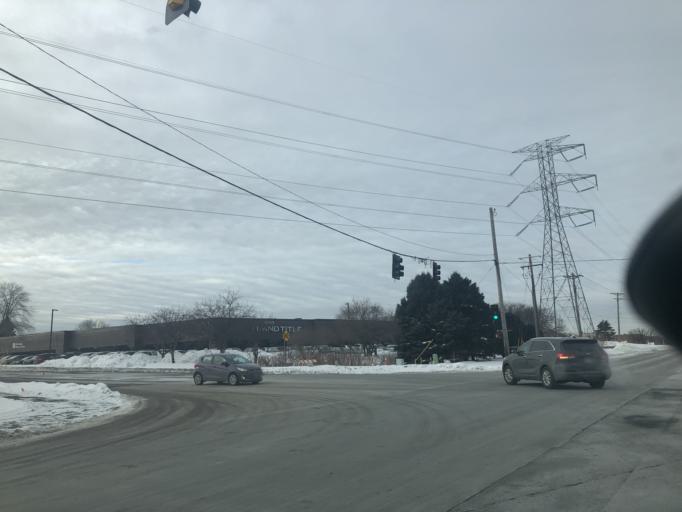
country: US
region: Minnesota
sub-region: Hennepin County
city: Saint Anthony
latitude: 45.0206
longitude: -93.1924
